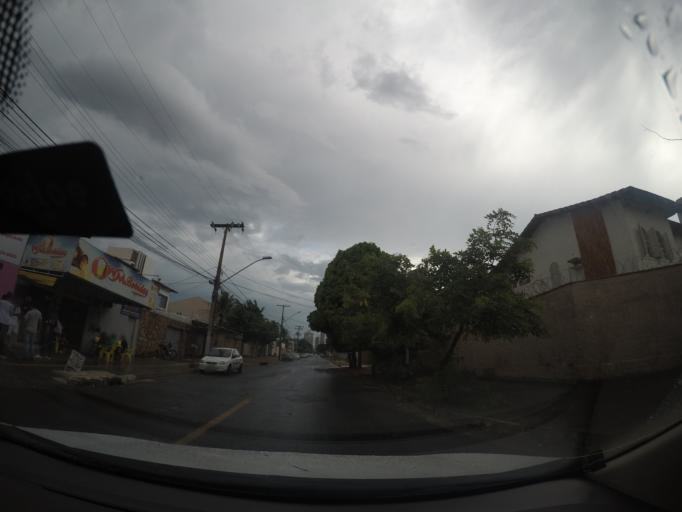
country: BR
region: Goias
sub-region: Goiania
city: Goiania
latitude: -16.7122
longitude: -49.2801
